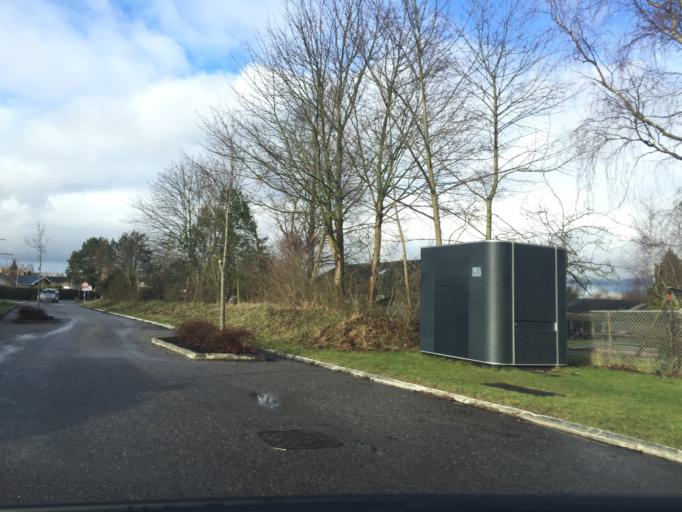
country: DK
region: Capital Region
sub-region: Fureso Kommune
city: Stavnsholt
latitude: 55.8115
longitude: 12.3992
